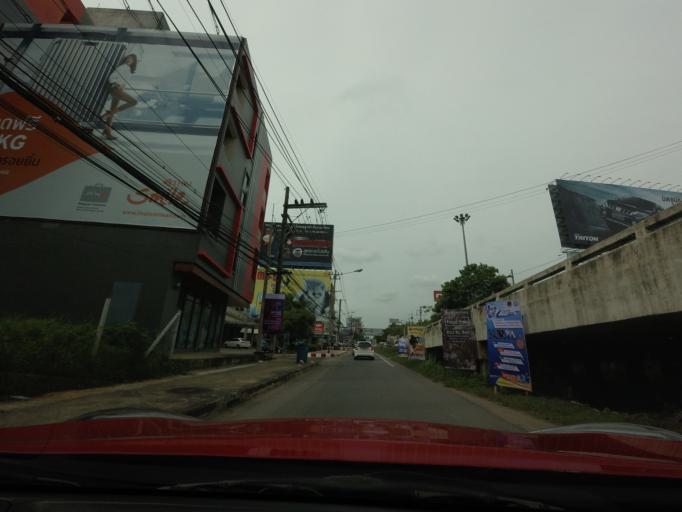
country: TH
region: Songkhla
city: Hat Yai
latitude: 6.9894
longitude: 100.4835
